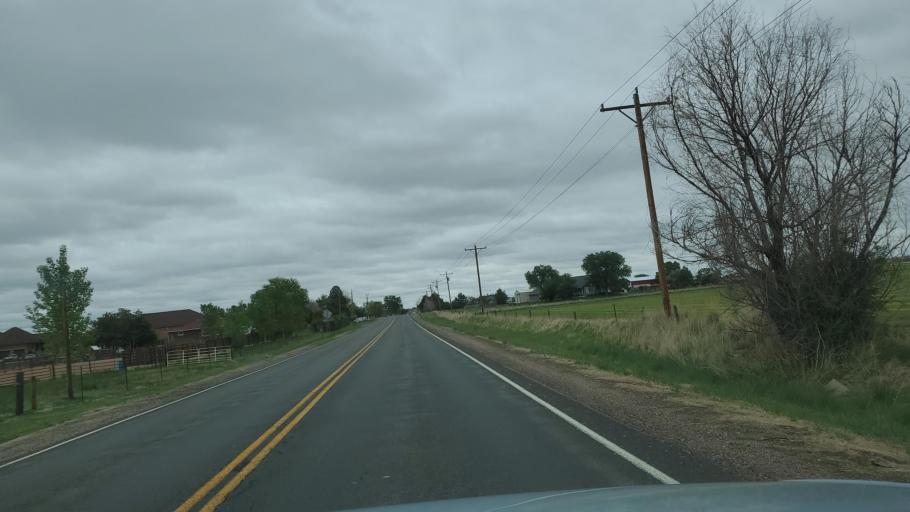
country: US
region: Colorado
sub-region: Weld County
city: Lochbuie
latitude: 39.9724
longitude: -104.7131
